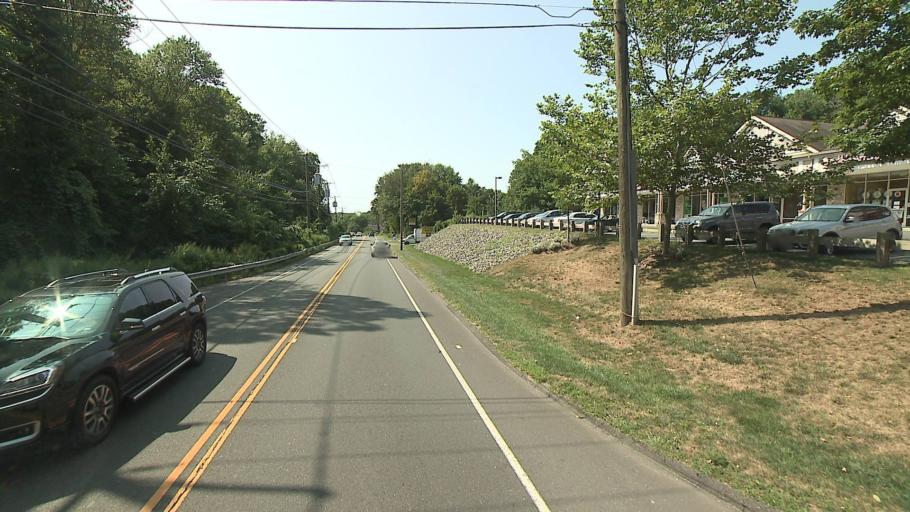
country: US
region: Connecticut
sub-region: Fairfield County
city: Newtown
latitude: 41.3284
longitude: -73.2664
